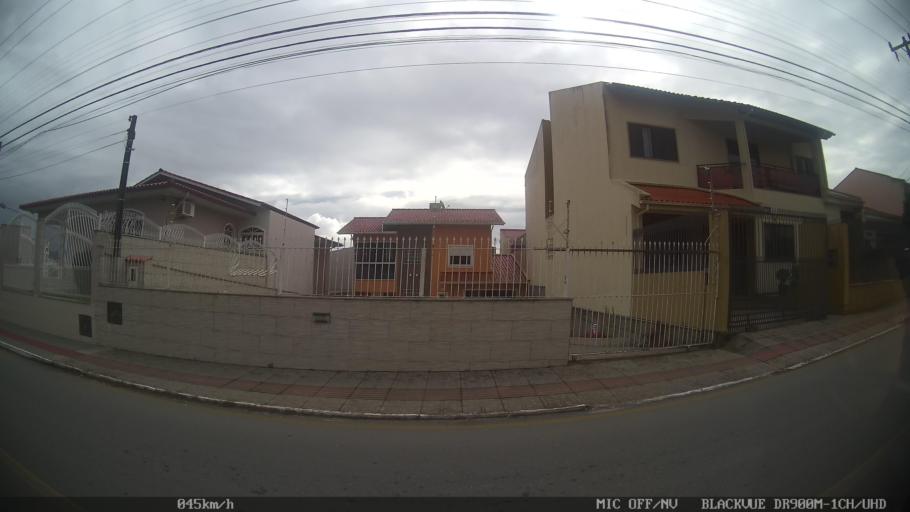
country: BR
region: Santa Catarina
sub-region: Sao Jose
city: Campinas
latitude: -27.5664
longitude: -48.6276
